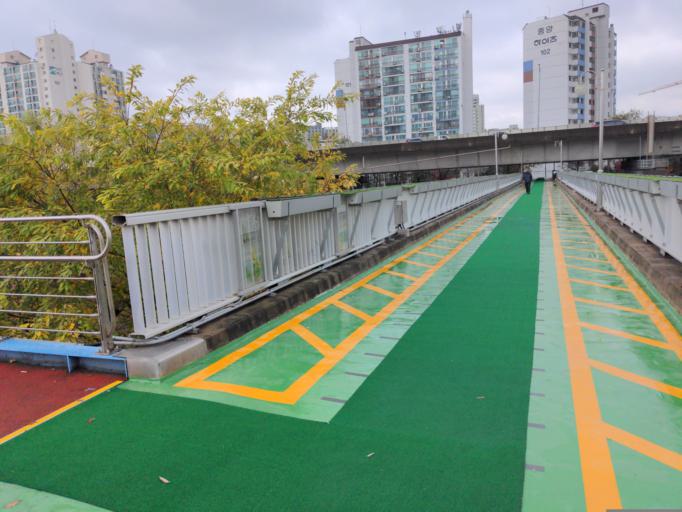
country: KR
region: Seoul
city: Seoul
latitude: 37.5627
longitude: 127.0505
